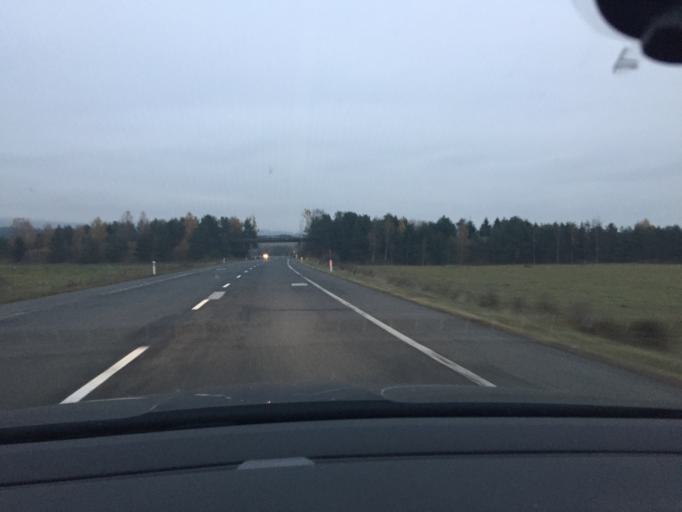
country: SK
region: Presovsky
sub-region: Okres Poprad
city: Nova Lesna
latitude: 49.0971
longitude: 20.2600
